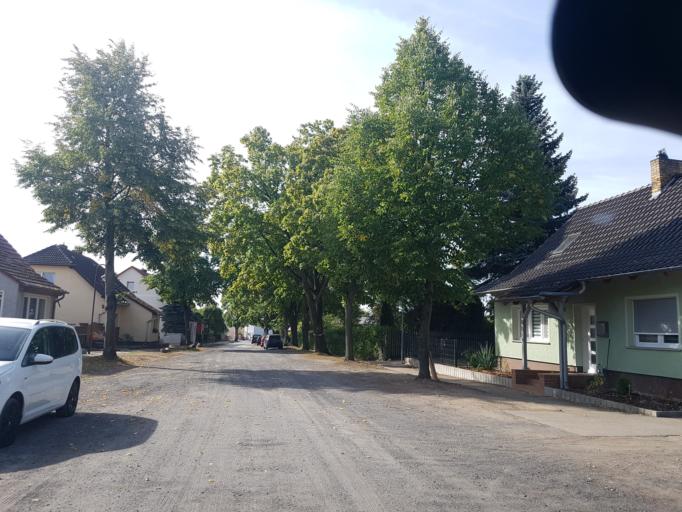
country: DE
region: Brandenburg
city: Wiesenburg
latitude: 52.1171
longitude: 12.4549
